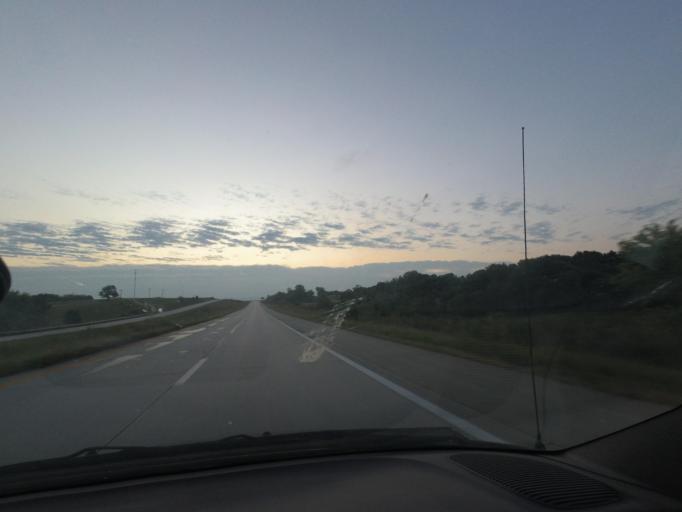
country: US
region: Missouri
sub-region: Linn County
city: Marceline
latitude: 39.7650
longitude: -92.7618
